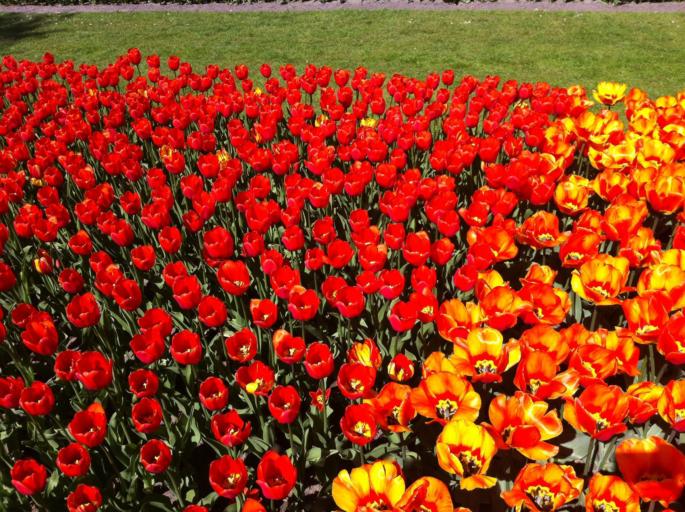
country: DK
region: Zealand
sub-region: Naestved Kommune
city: Naestved
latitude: 55.1890
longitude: 11.7238
